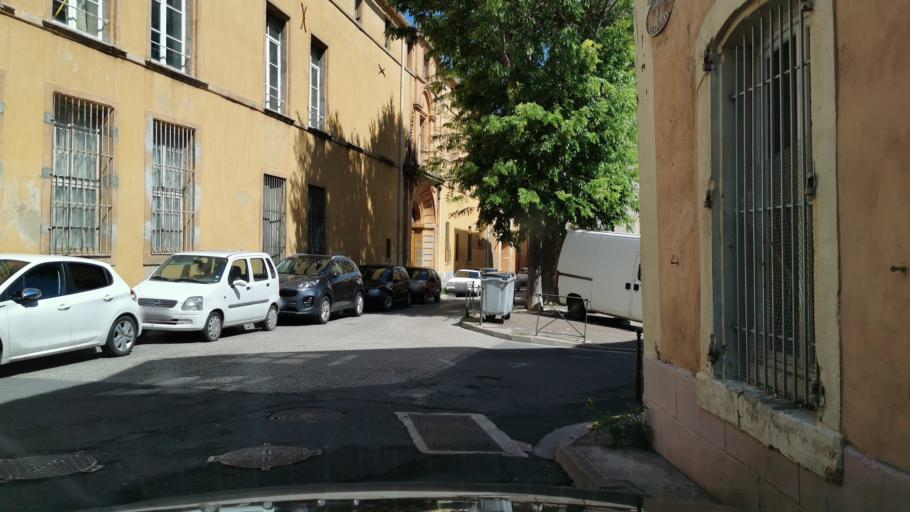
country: FR
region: Languedoc-Roussillon
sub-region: Departement de l'Aude
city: Narbonne
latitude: 43.1850
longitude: 3.0061
